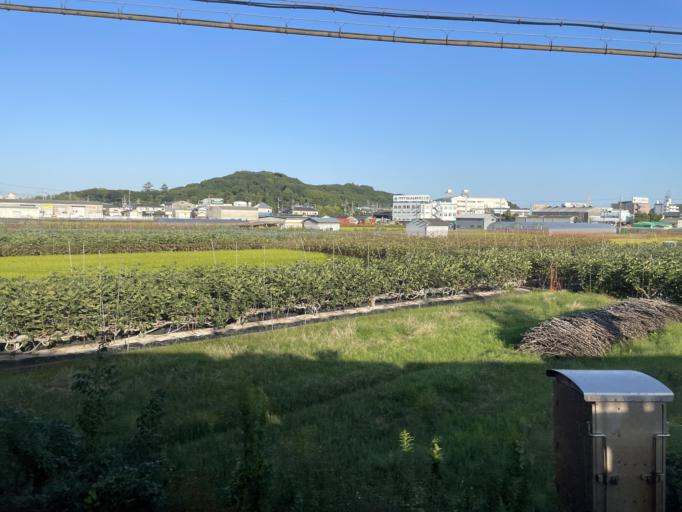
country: JP
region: Osaka
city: Kashihara
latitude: 34.5589
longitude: 135.6154
